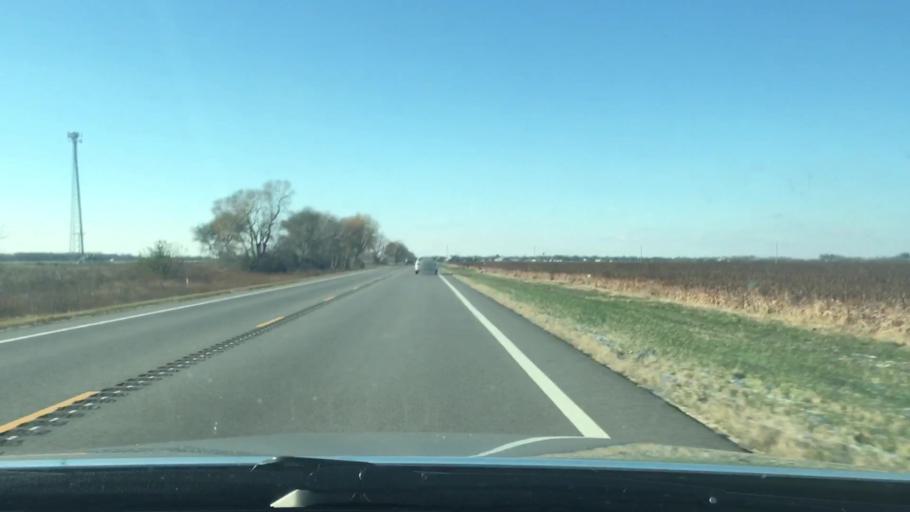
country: US
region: Kansas
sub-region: Reno County
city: Nickerson
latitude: 38.1268
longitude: -98.0537
